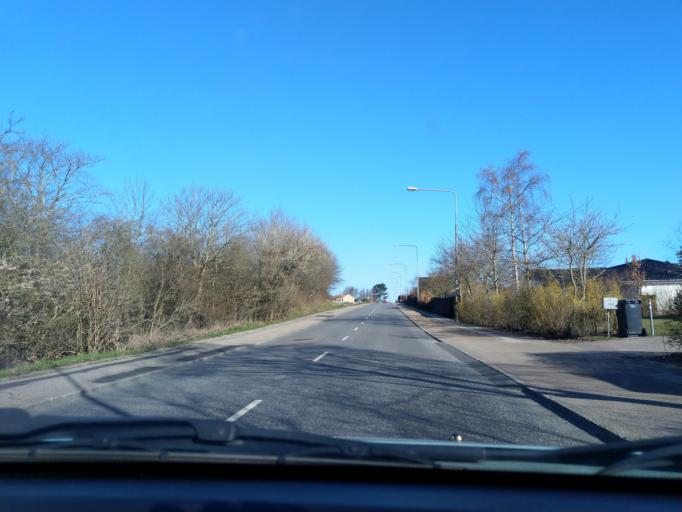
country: DK
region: Zealand
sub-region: Kalundborg Kommune
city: Kalundborg
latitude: 55.7062
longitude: 11.0228
